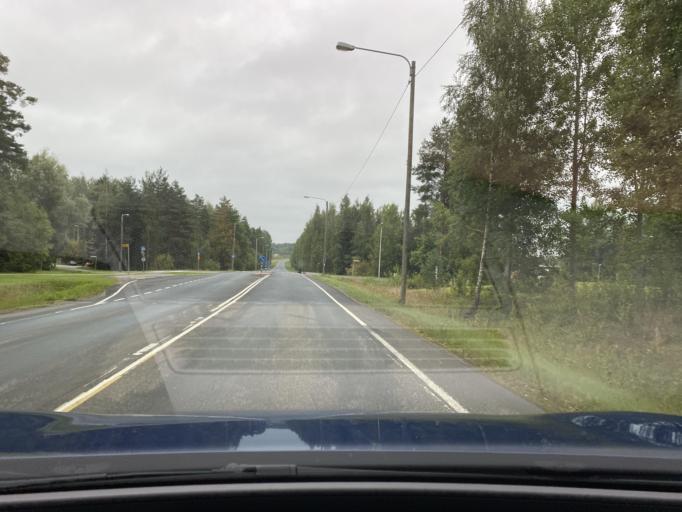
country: FI
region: Kymenlaakso
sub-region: Kouvola
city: Kouvola
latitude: 60.8949
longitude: 26.6040
